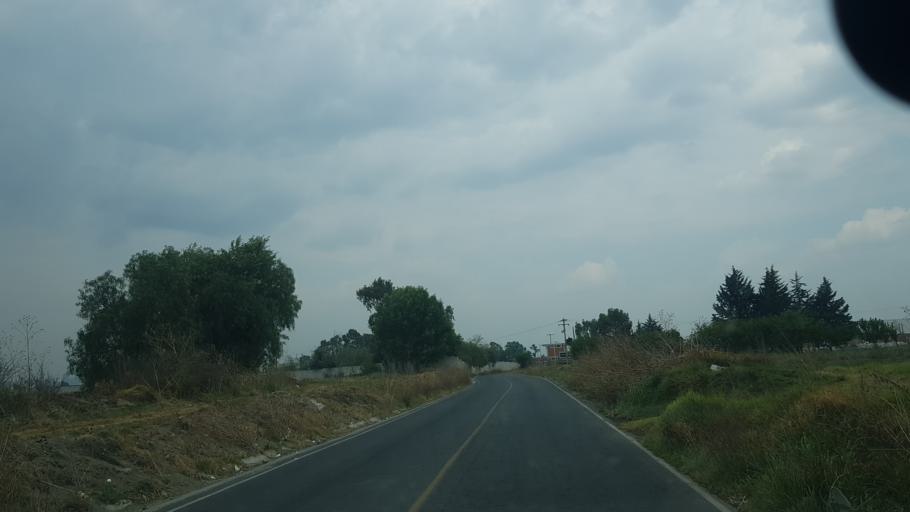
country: MX
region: Puebla
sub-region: Huejotzingo
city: San Mateo Capultitlan
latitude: 19.2031
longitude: -98.4271
